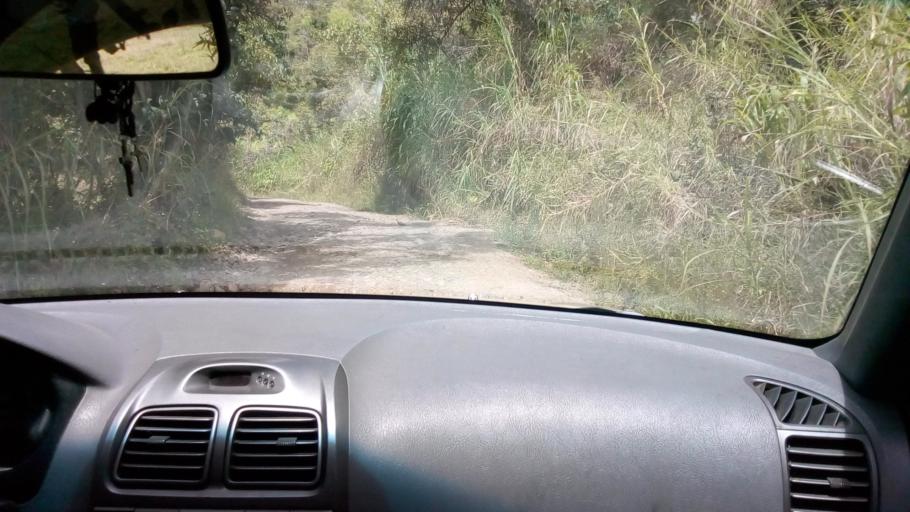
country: CO
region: Cundinamarca
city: Tenza
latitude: 5.0923
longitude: -73.4222
